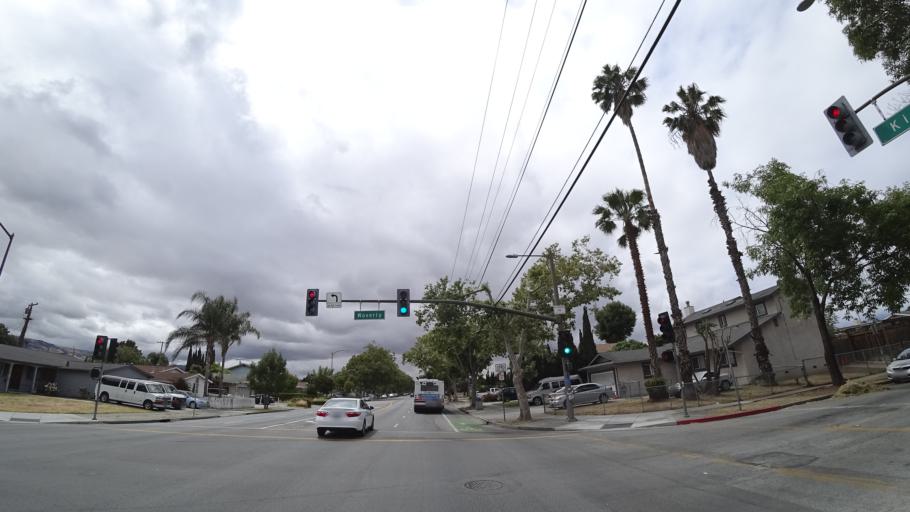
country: US
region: California
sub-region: Santa Clara County
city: Alum Rock
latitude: 37.3258
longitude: -121.8294
